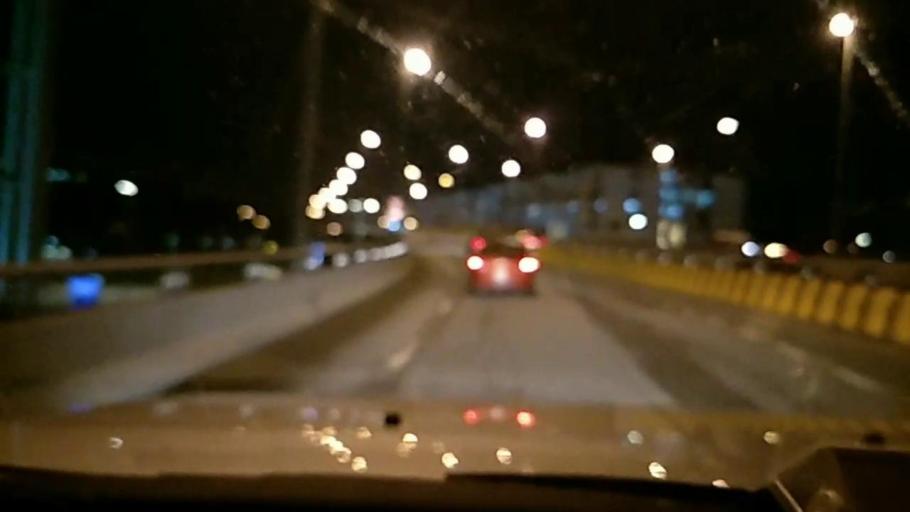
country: MY
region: Kuala Lumpur
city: Kuala Lumpur
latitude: 3.1353
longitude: 101.7200
